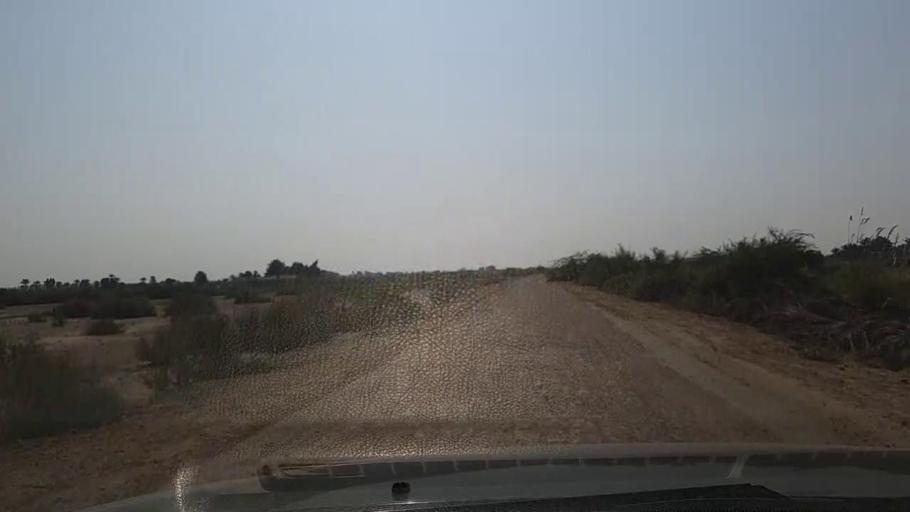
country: PK
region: Sindh
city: Mirpur Sakro
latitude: 24.3839
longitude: 67.6623
